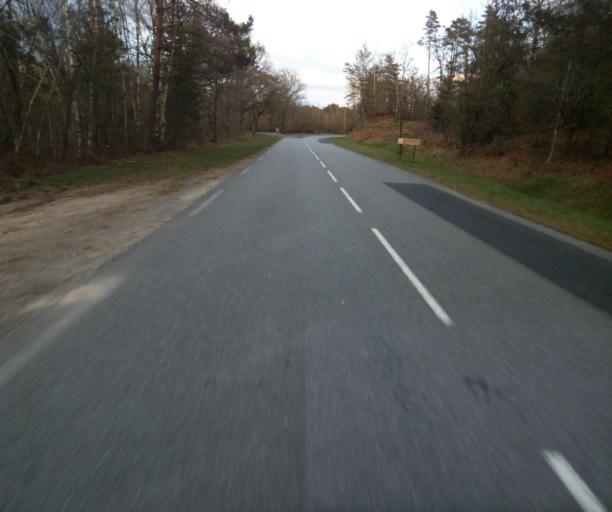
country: FR
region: Limousin
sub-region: Departement de la Correze
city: Correze
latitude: 45.2835
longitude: 1.9200
